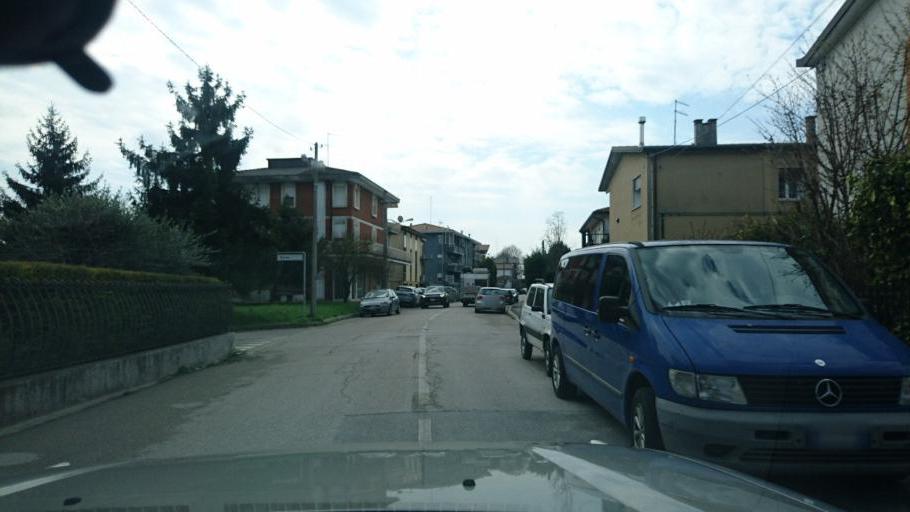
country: IT
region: Veneto
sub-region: Provincia di Padova
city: Noventa
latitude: 45.4005
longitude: 11.9437
